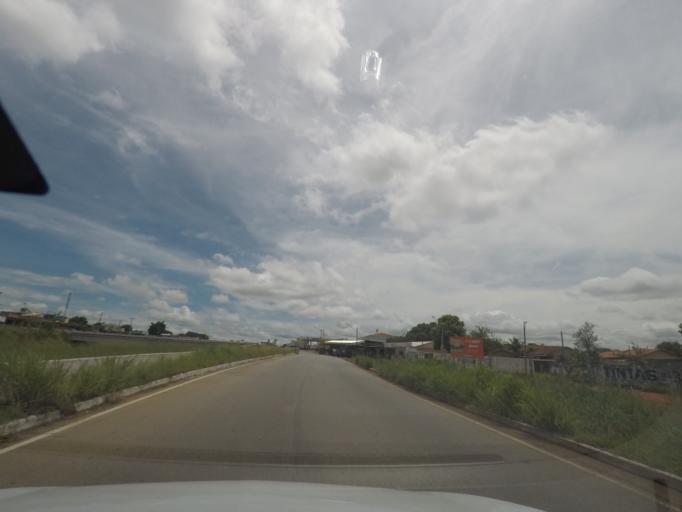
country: BR
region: Goias
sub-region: Goiania
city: Goiania
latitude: -16.7207
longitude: -49.3722
